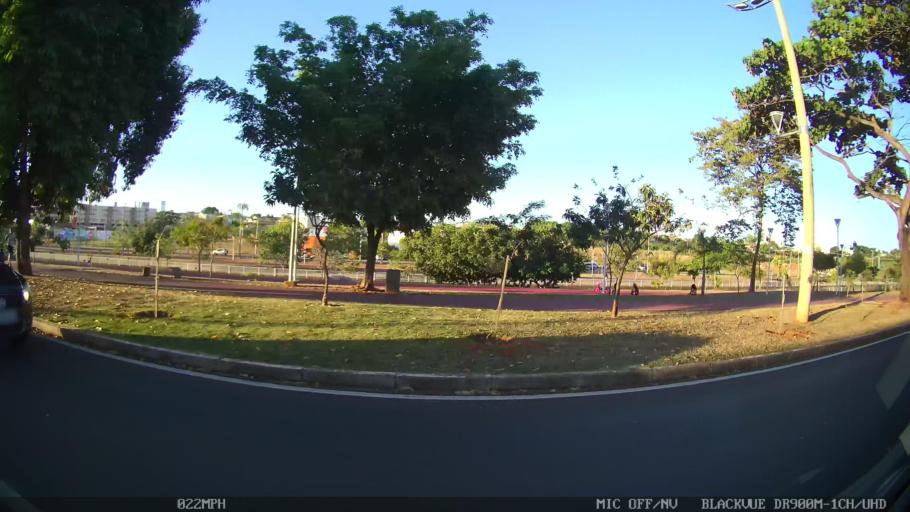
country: BR
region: Sao Paulo
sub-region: Sao Jose Do Rio Preto
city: Sao Jose do Rio Preto
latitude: -20.7852
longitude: -49.3782
